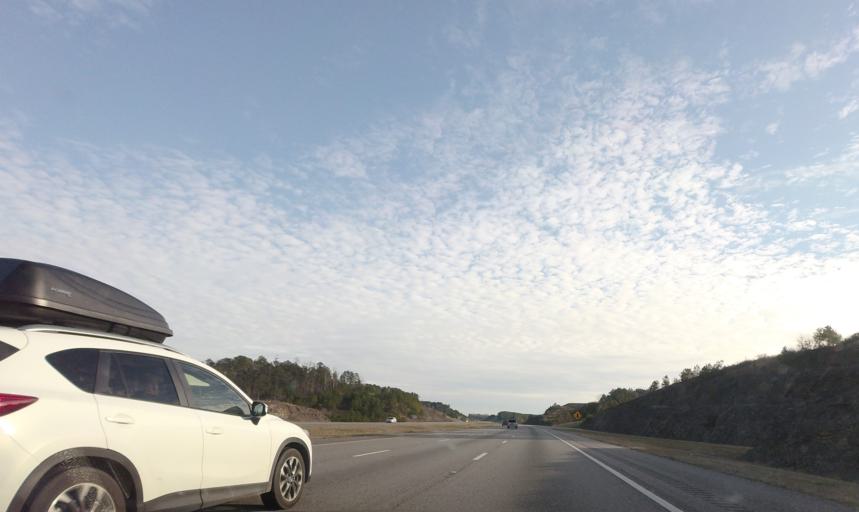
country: US
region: Alabama
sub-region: Walker County
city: Cordova
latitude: 33.7392
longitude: -87.1999
